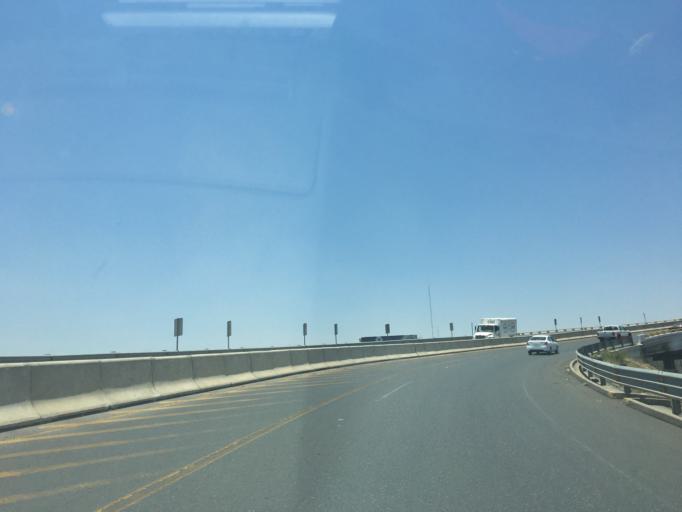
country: MX
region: Zacatecas
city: Zacatecas
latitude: 22.7735
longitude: -102.6214
